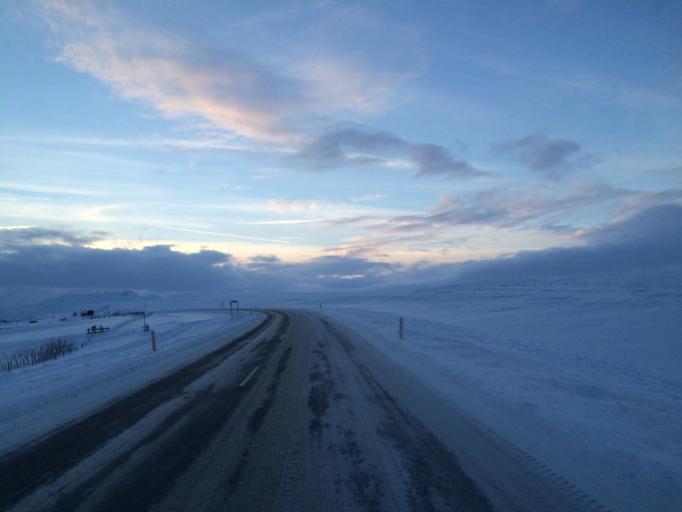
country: IS
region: South
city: Hveragerdi
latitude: 64.2342
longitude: -21.1956
